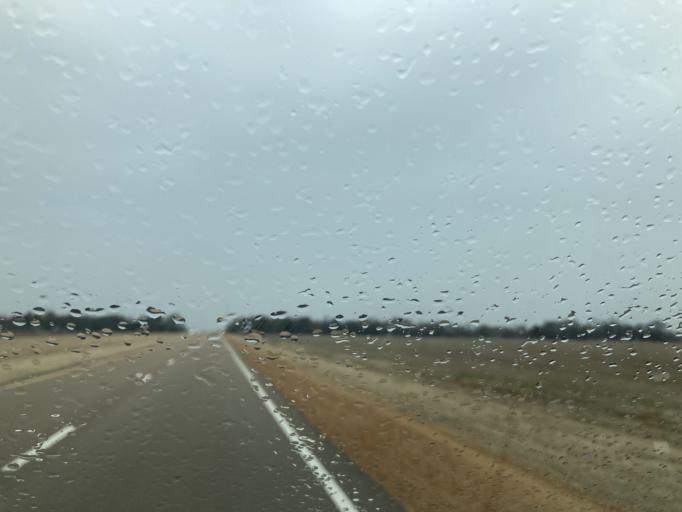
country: US
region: Mississippi
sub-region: Humphreys County
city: Belzoni
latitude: 33.0873
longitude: -90.4878
